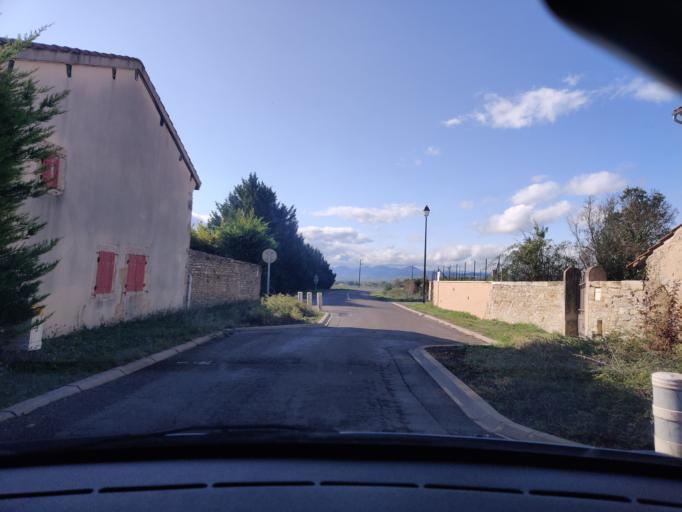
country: FR
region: Auvergne
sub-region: Departement du Puy-de-Dome
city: Aigueperse
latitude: 46.0057
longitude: 3.1666
